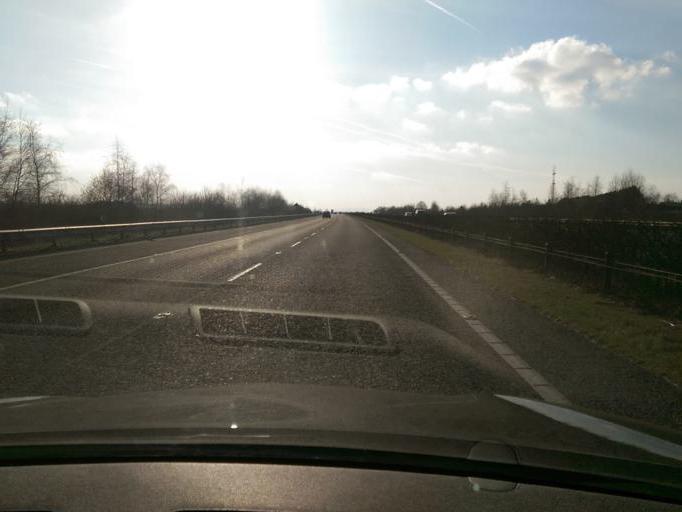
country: IE
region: Leinster
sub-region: Kildare
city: Cherryville
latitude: 53.1540
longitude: -6.9579
